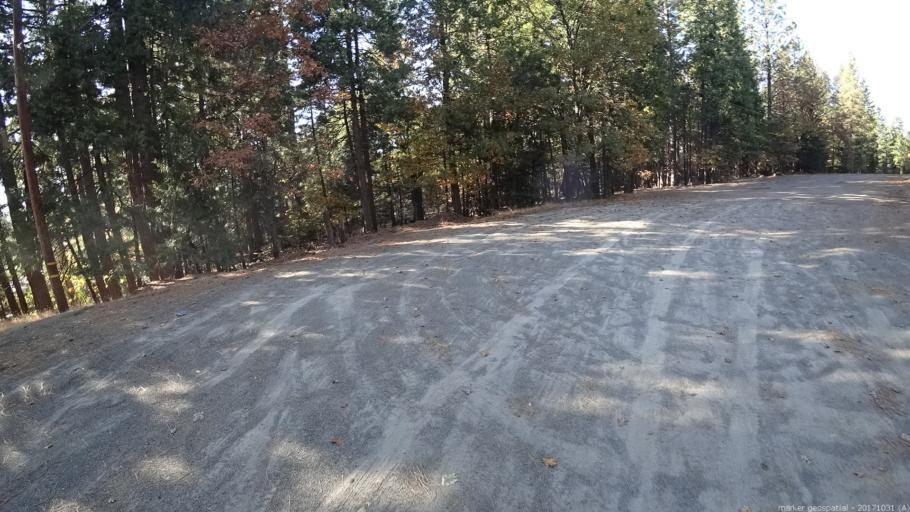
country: US
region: California
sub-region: Shasta County
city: Shingletown
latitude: 40.4982
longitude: -121.9156
